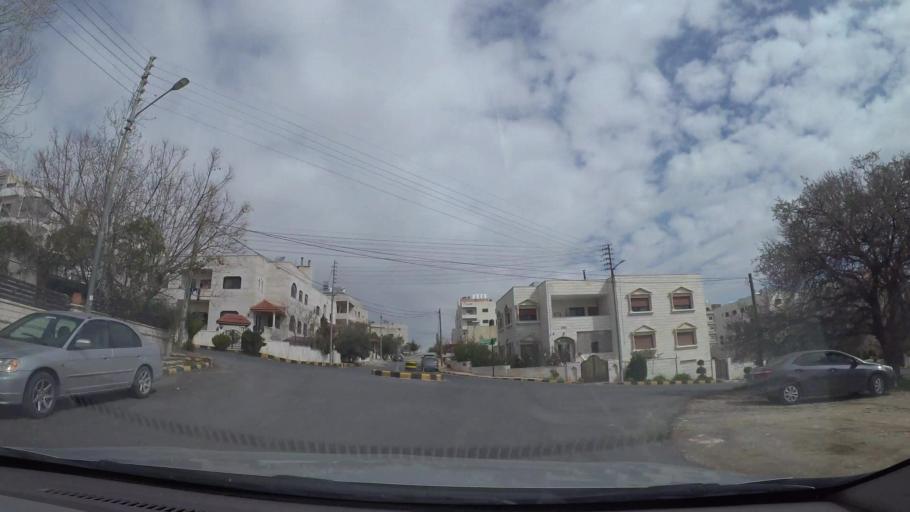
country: JO
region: Amman
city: Al Jubayhah
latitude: 32.0018
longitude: 35.8344
